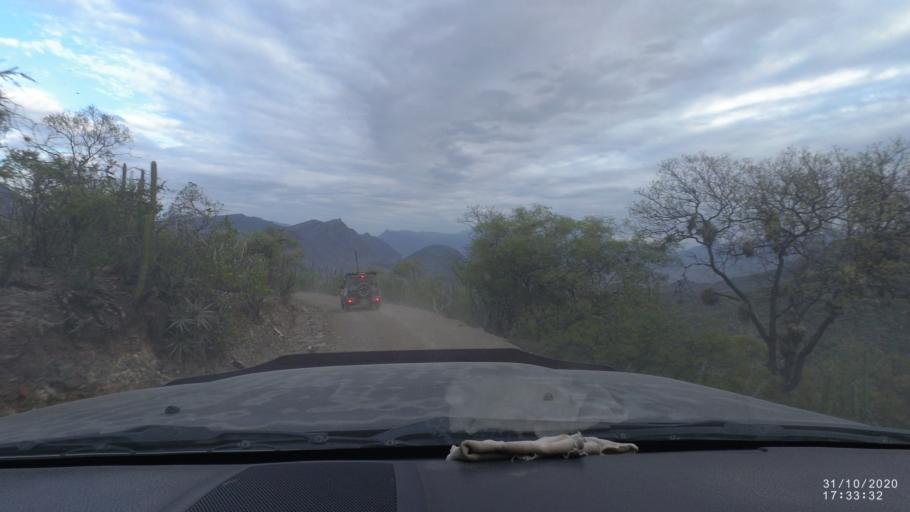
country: BO
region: Chuquisaca
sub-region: Provincia Zudanez
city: Mojocoya
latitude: -18.6004
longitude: -64.5501
